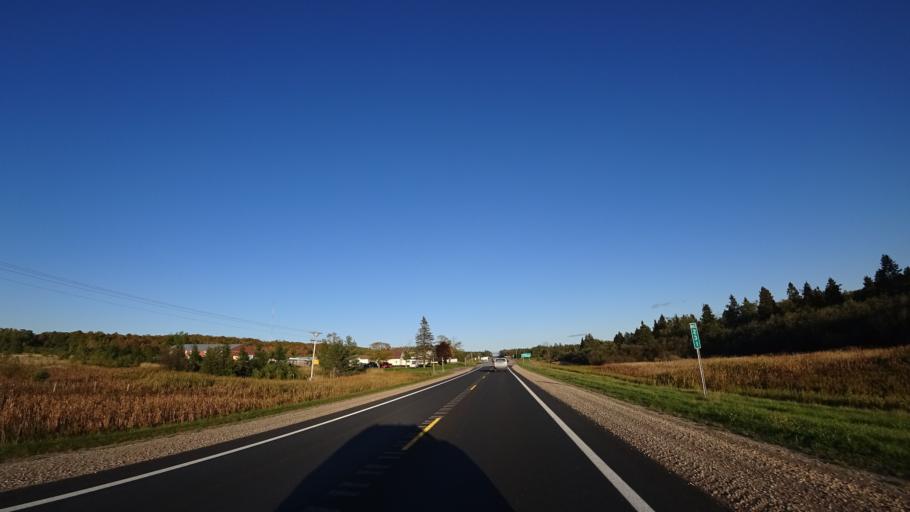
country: US
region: Michigan
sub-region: Luce County
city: Newberry
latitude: 46.3104
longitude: -85.5713
